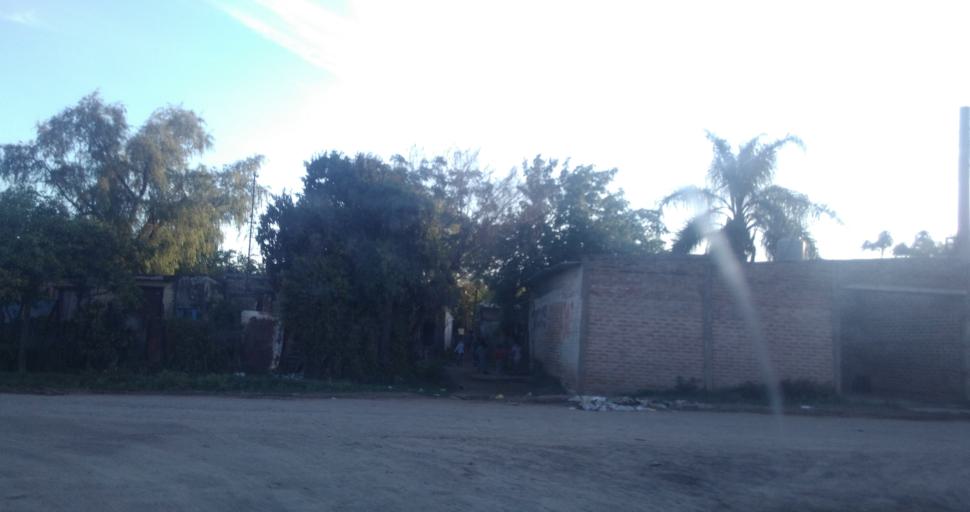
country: AR
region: Chaco
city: Fontana
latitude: -27.4300
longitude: -59.0021
